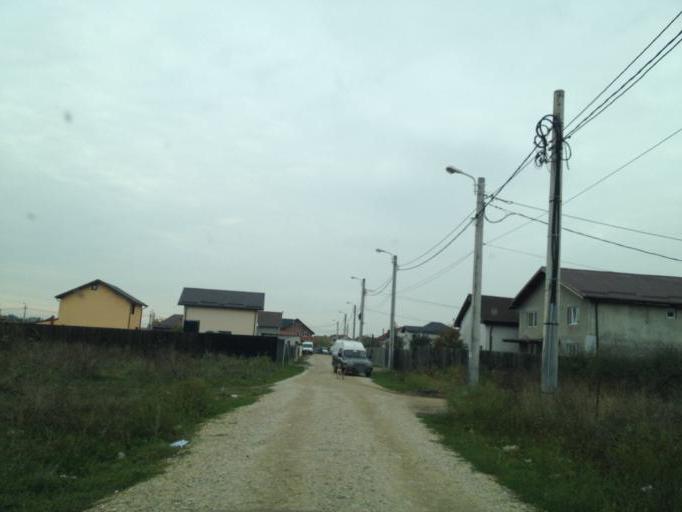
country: RO
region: Dolj
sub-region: Municipiul Craiova
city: Popoveni
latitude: 44.2950
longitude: 23.7805
